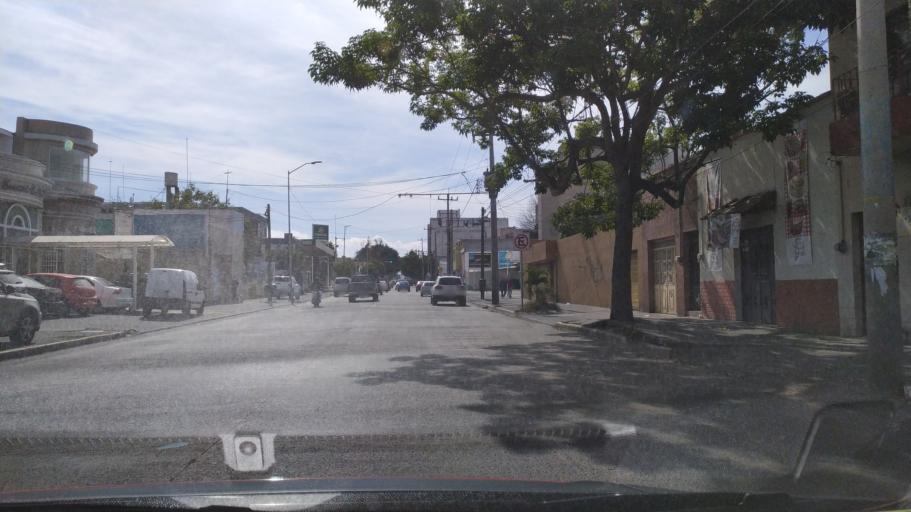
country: MX
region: Jalisco
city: Tlaquepaque
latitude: 20.6752
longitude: -103.3296
